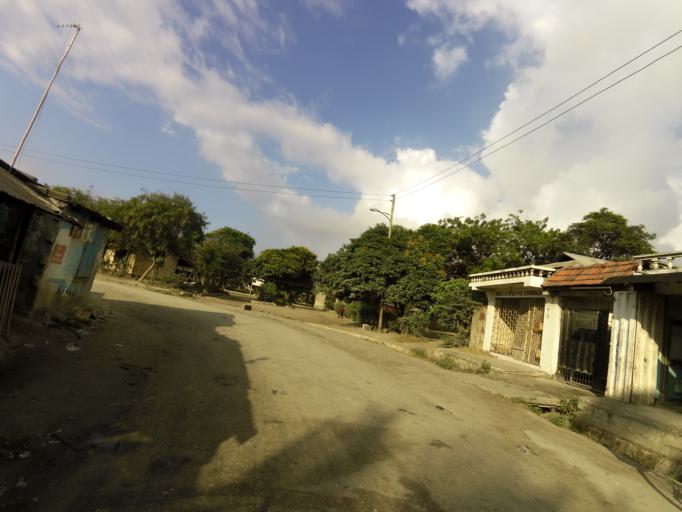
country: TZ
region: Dar es Salaam
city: Magomeni
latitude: -6.7902
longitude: 39.2304
